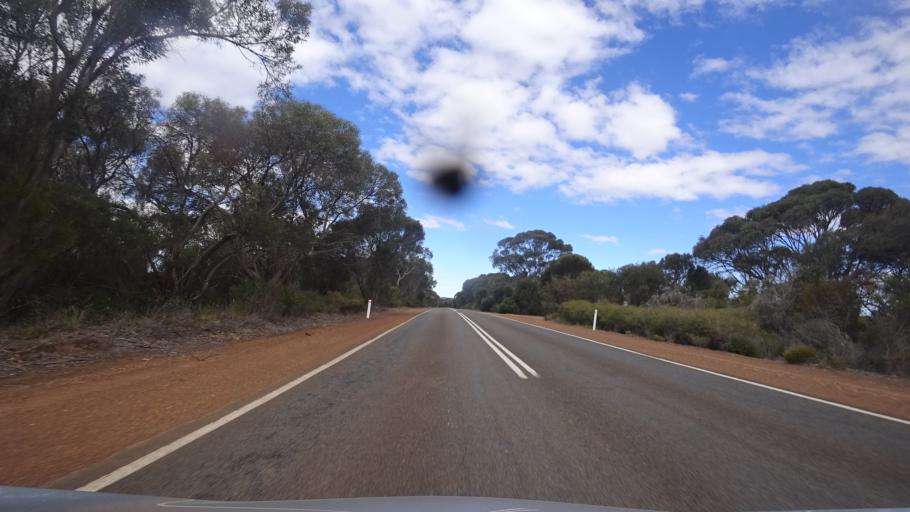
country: AU
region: South Australia
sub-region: Kangaroo Island
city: Kingscote
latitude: -35.7611
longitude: 137.3714
